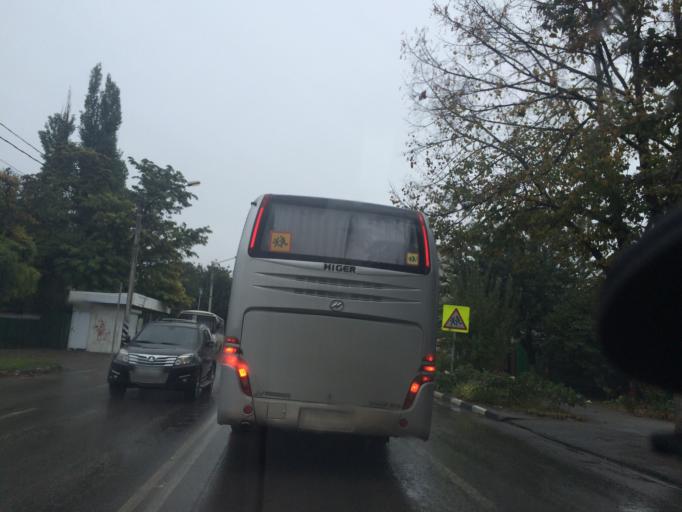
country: RU
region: Rostov
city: Azov
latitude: 47.0938
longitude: 39.4490
